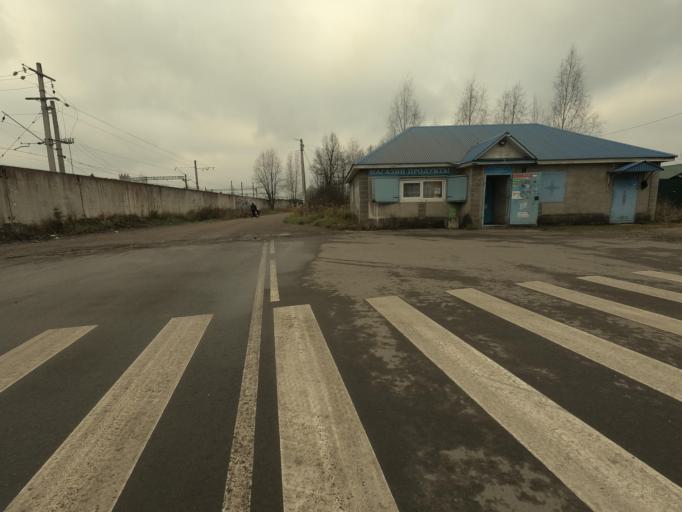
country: RU
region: Leningrad
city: Lyuban'
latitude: 59.4961
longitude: 31.2750
